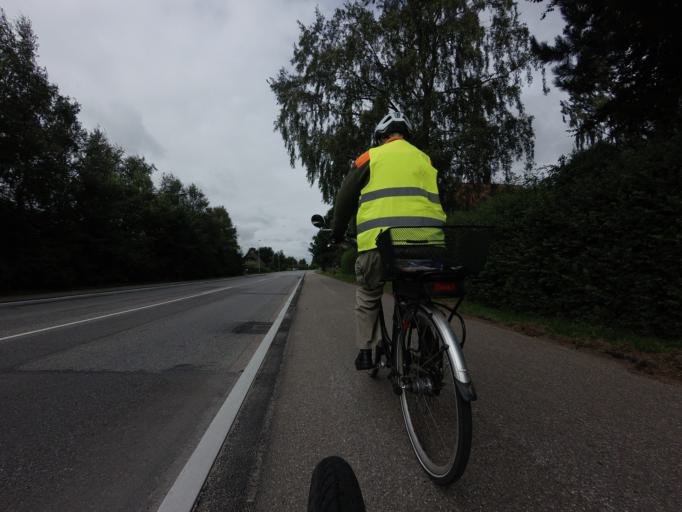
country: DK
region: Central Jutland
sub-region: Syddjurs Kommune
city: Ryomgard
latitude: 56.3826
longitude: 10.4830
